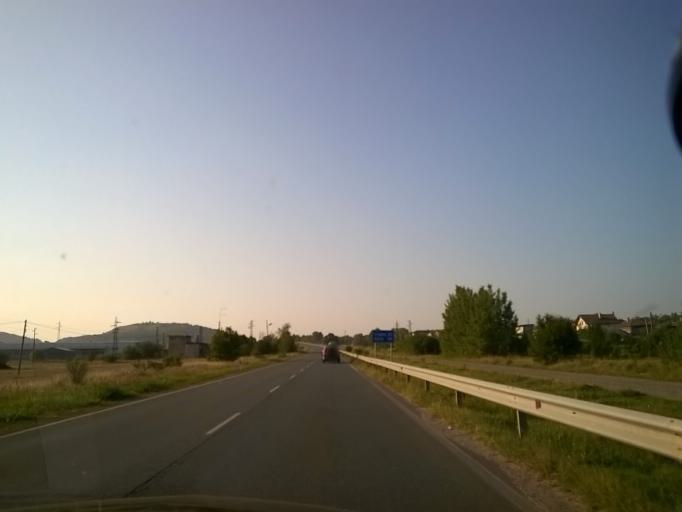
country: BG
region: Sofiya
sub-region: Obshtina Dragoman
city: Dragoman
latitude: 42.9178
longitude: 22.9389
